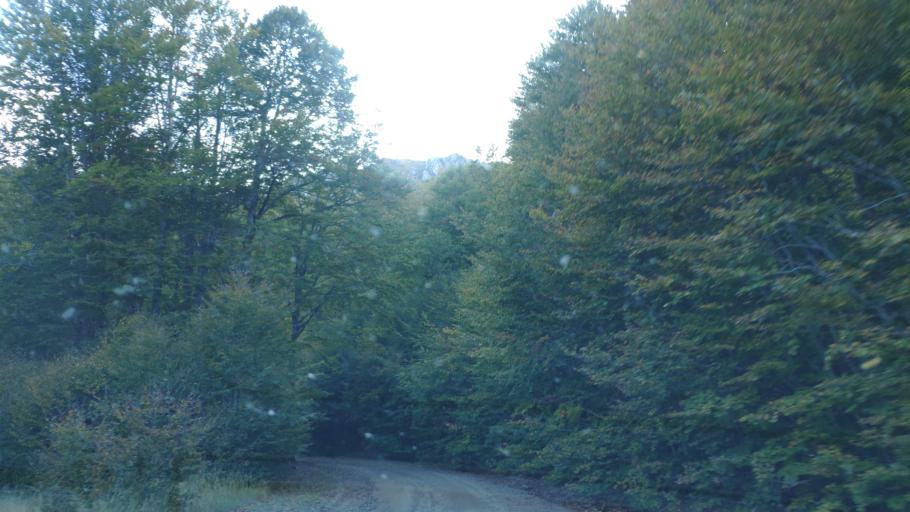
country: GR
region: West Macedonia
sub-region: Nomos Kastorias
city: Nestorio
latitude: 40.3265
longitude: 20.9018
